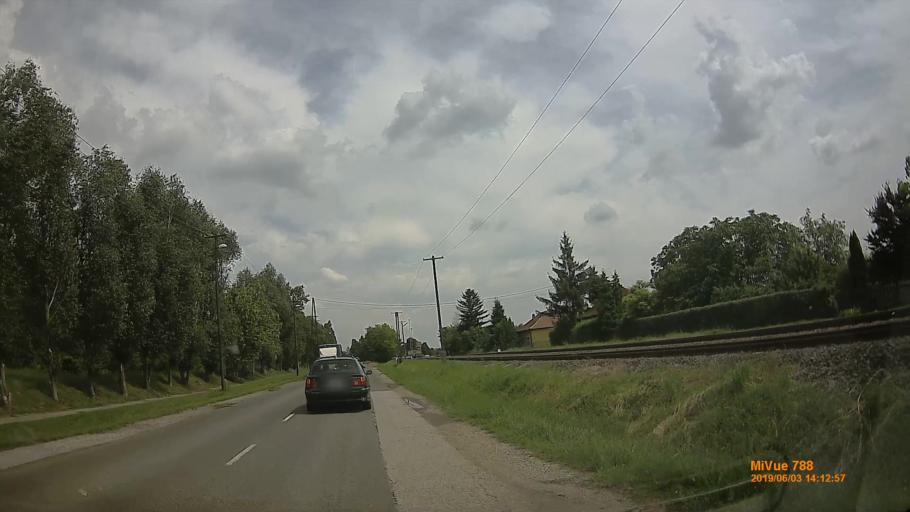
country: HU
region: Jasz-Nagykun-Szolnok
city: Toszeg
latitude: 47.1005
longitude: 20.1339
